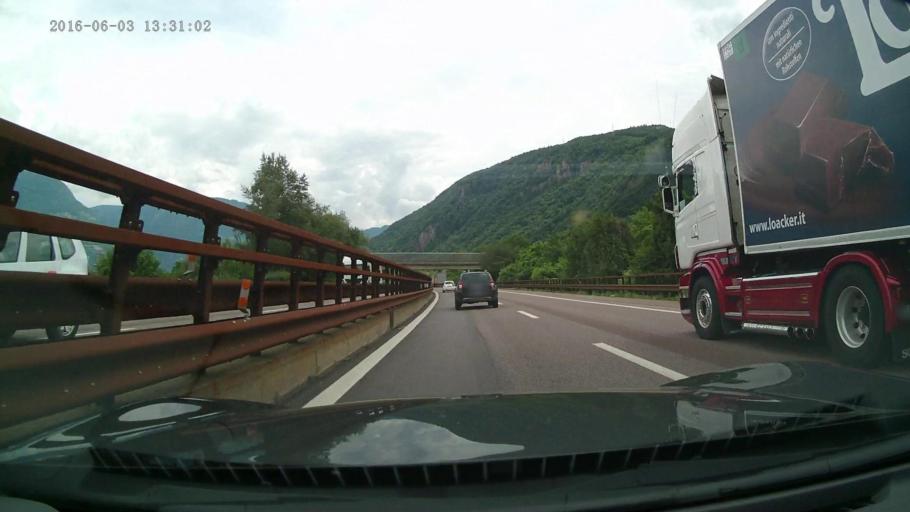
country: IT
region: Trentino-Alto Adige
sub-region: Bolzano
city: Cornaiano
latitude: 46.4569
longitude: 11.3042
